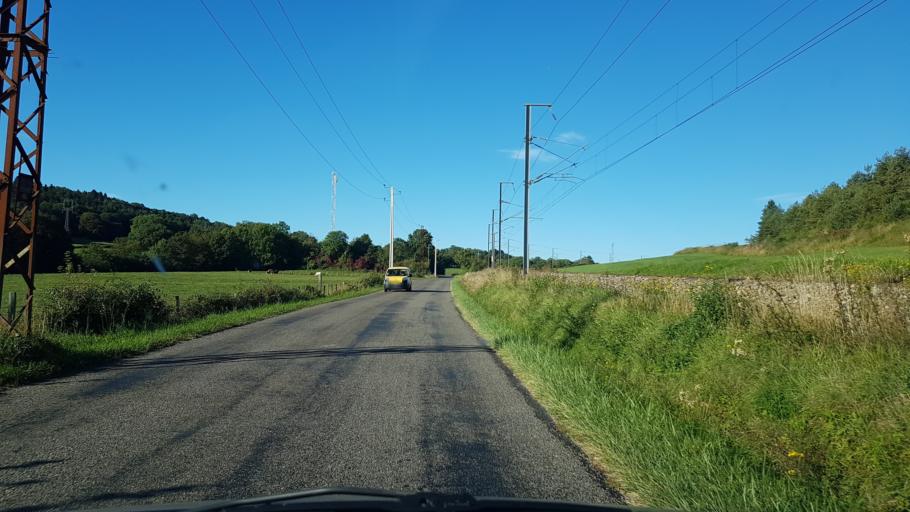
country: FR
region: Rhone-Alpes
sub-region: Departement de l'Ain
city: Villereversure
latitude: 46.1606
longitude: 5.3549
